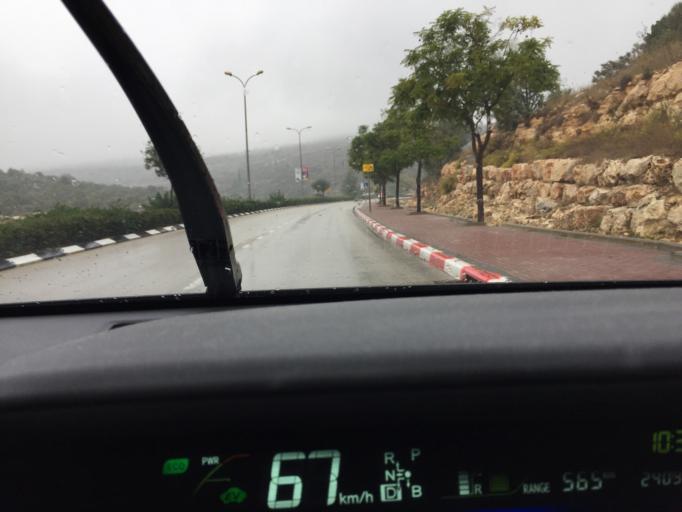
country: IL
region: Jerusalem
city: Ariel
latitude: 32.1007
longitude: 35.1659
